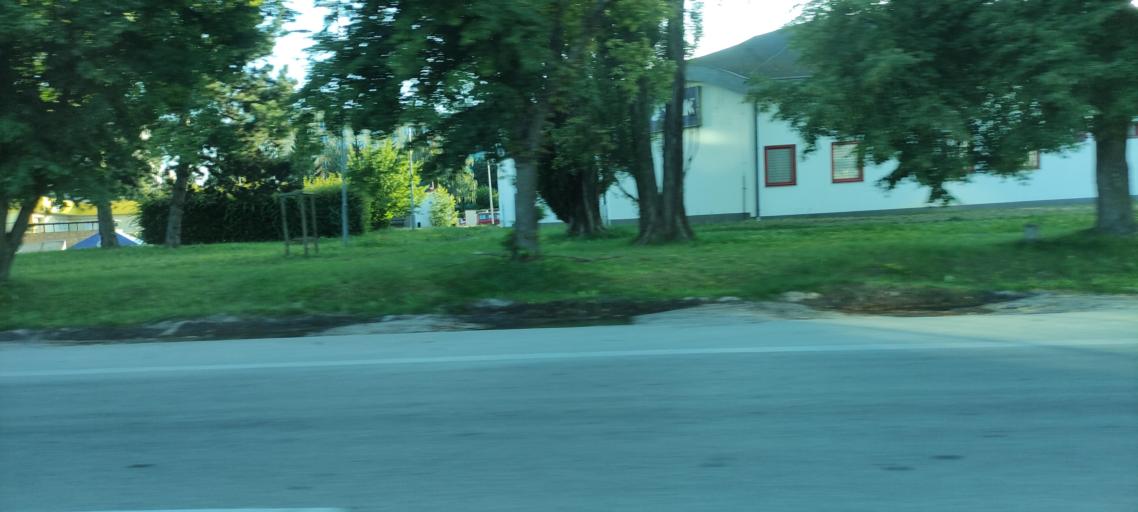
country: CZ
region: Jihocesky
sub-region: Okres Jindrichuv Hradec
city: Jindrichuv Hradec
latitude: 49.1429
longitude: 15.0241
